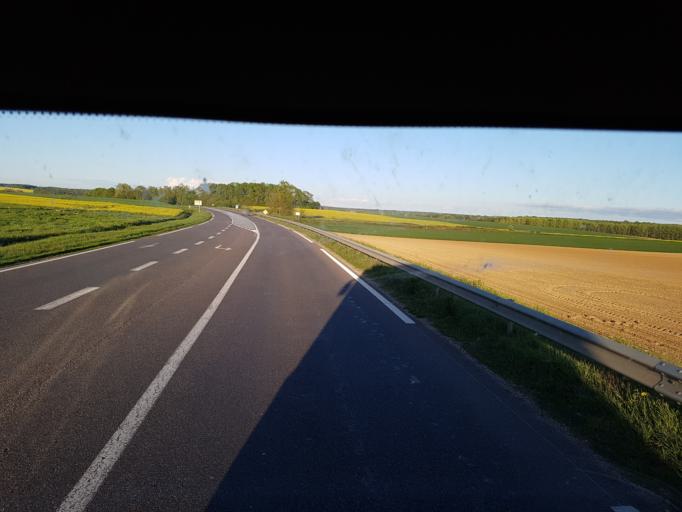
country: FR
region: Champagne-Ardenne
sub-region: Departement de la Marne
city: Esternay
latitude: 48.7187
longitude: 3.5480
